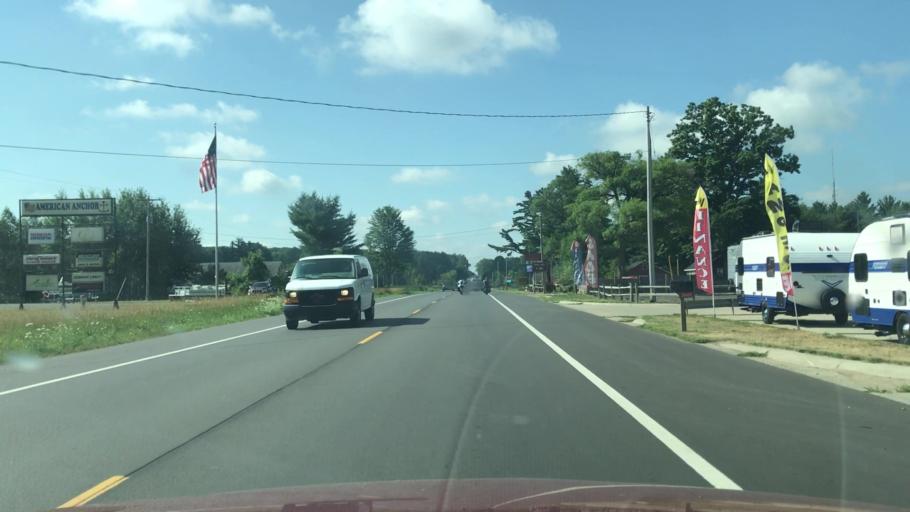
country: US
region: Michigan
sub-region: Newaygo County
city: Newaygo
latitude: 43.3974
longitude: -85.8008
